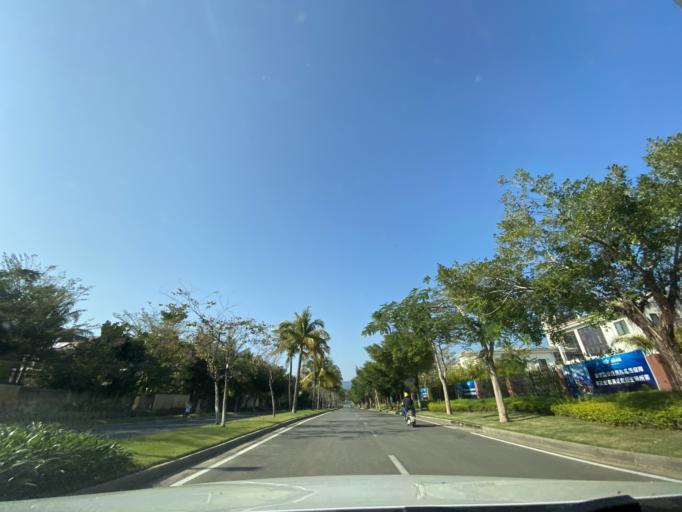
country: CN
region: Hainan
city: Yingzhou
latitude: 18.4154
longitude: 109.8892
